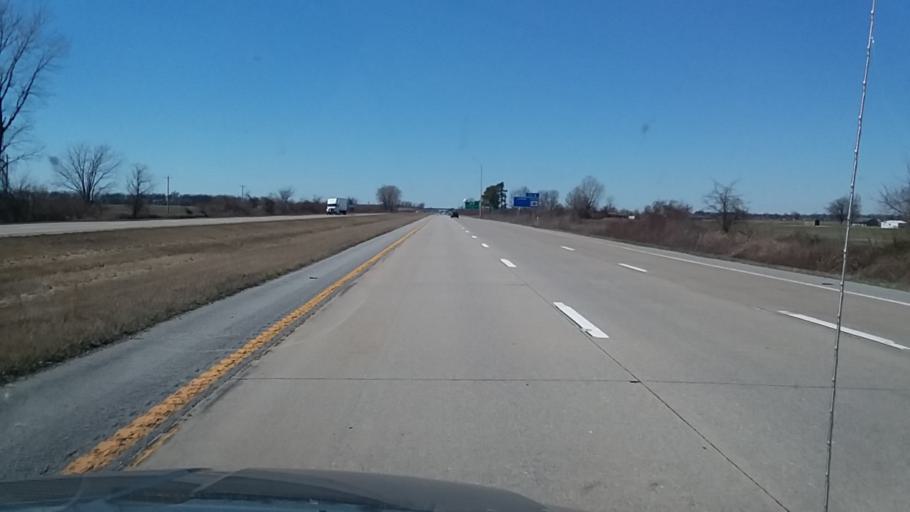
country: US
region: Missouri
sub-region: Pemiscot County
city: Caruthersville
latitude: 36.1441
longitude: -89.6463
